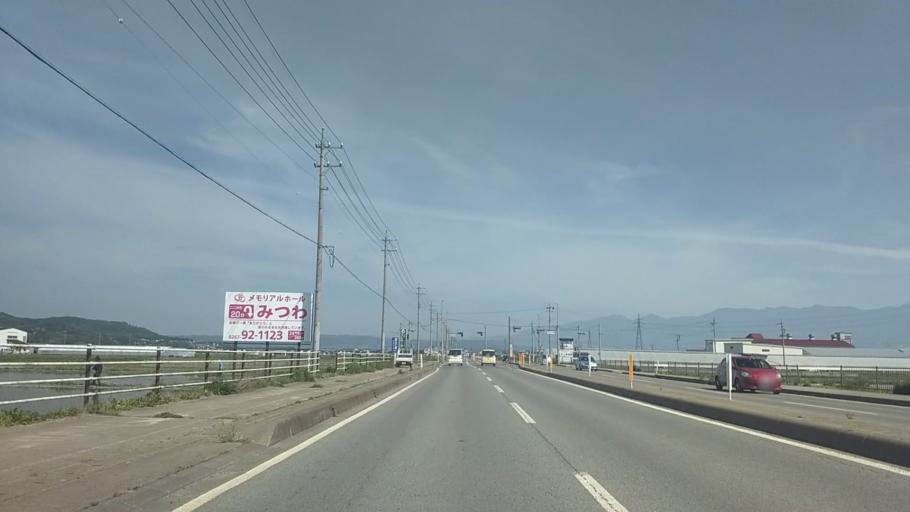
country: JP
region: Nagano
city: Saku
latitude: 36.2146
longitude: 138.4632
